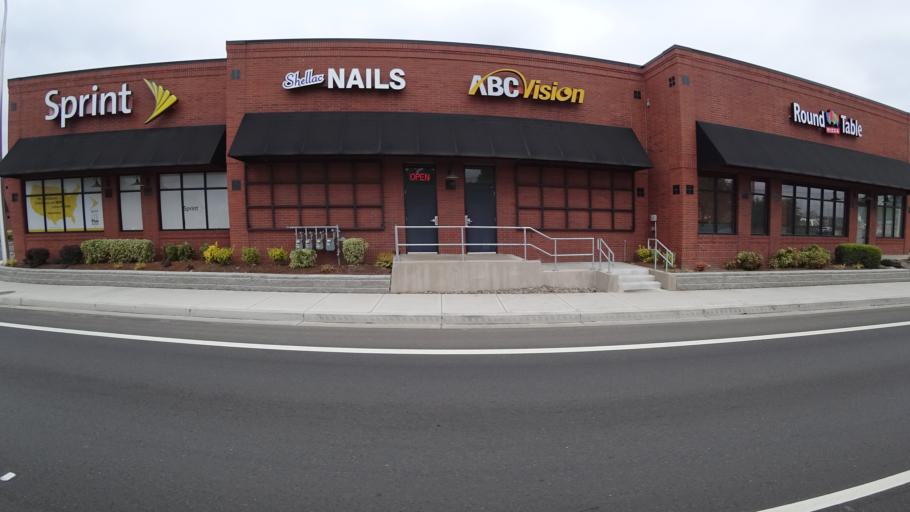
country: US
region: Oregon
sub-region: Washington County
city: Aloha
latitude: 45.4978
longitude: -122.9044
